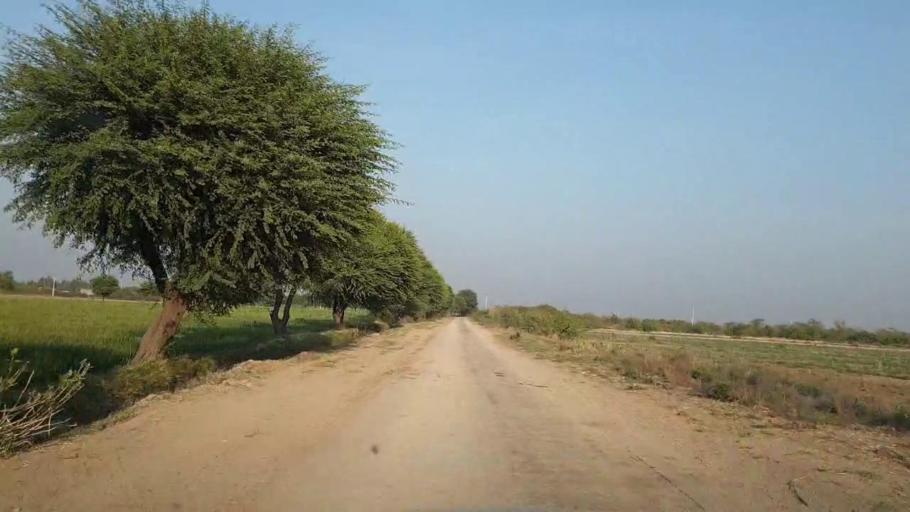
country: PK
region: Sindh
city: Mirpur Khas
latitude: 25.6723
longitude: 69.1969
